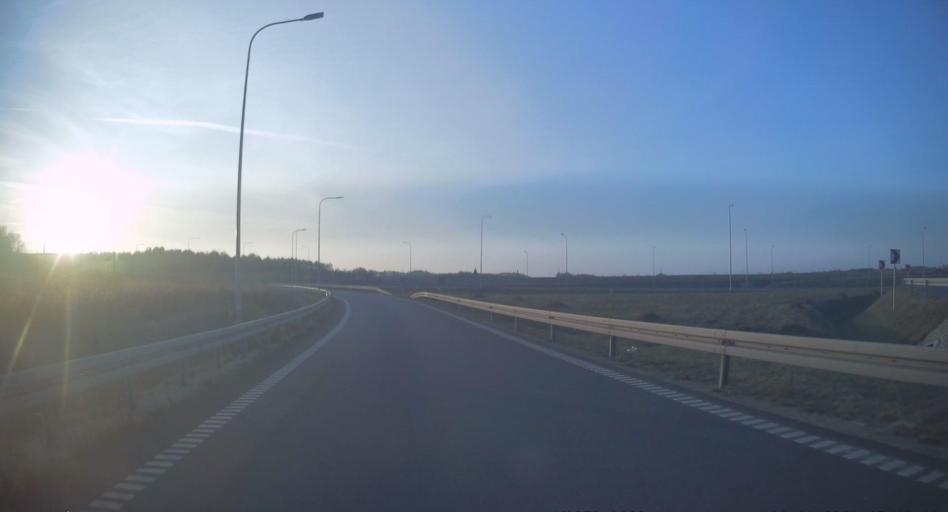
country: PL
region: Silesian Voivodeship
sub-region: Powiat klobucki
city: Kamyk
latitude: 50.8458
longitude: 19.0410
